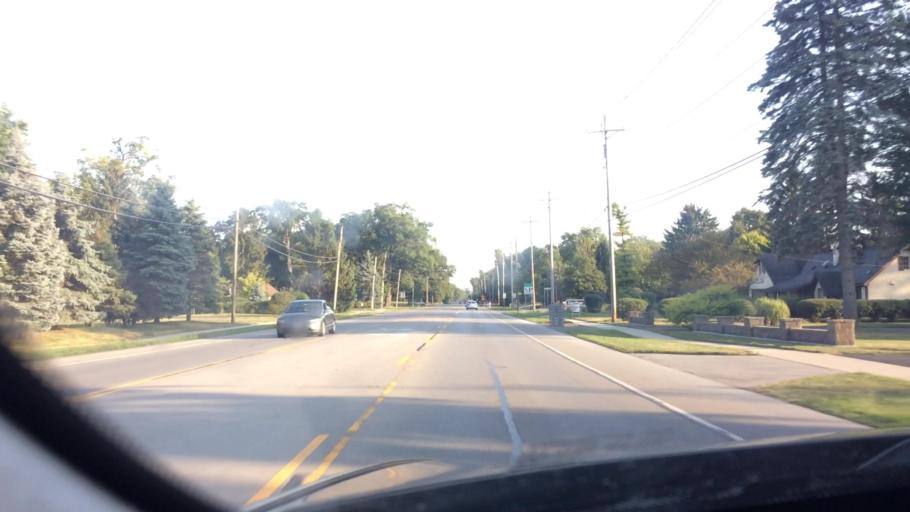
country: US
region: Ohio
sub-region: Lucas County
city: Sylvania
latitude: 41.6717
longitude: -83.7029
